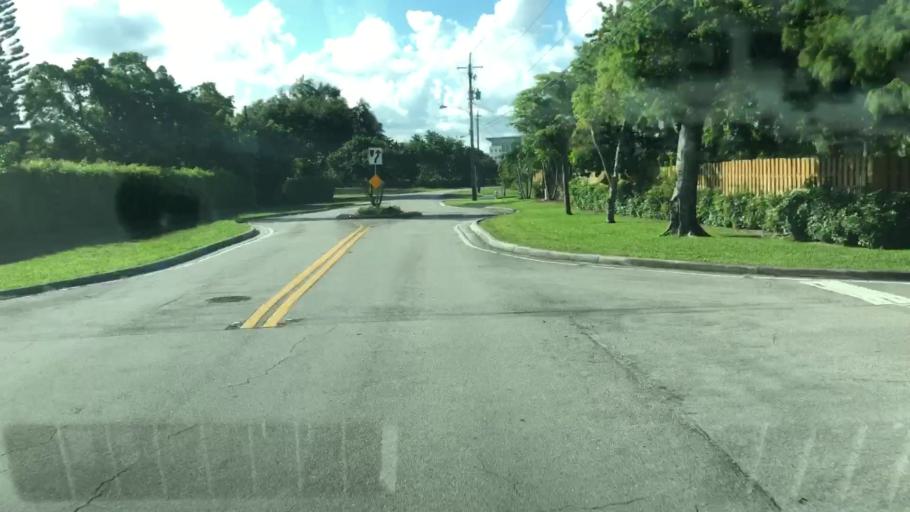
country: US
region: Florida
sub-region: Broward County
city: Coral Springs
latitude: 26.2758
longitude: -80.2555
